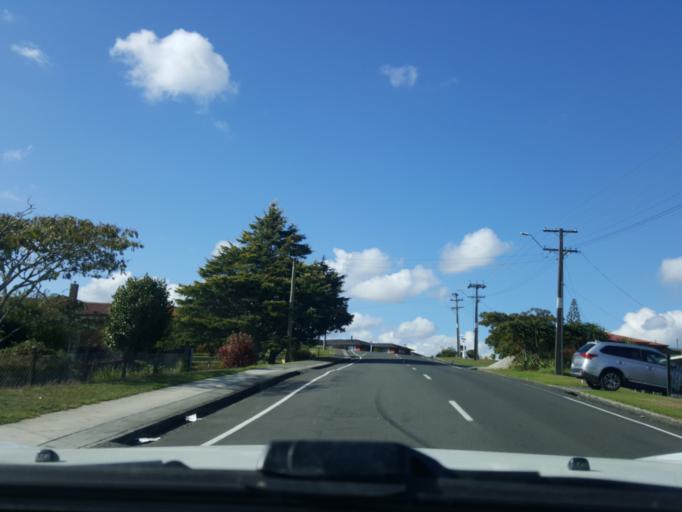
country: NZ
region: Waikato
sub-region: Waikato District
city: Ngaruawahia
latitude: -37.5474
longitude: 175.1668
